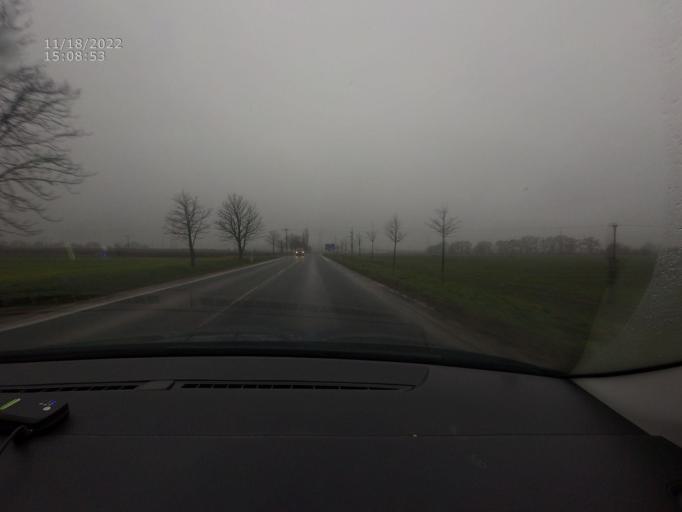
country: CZ
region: Jihocesky
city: Mirovice
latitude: 49.5178
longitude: 14.0822
